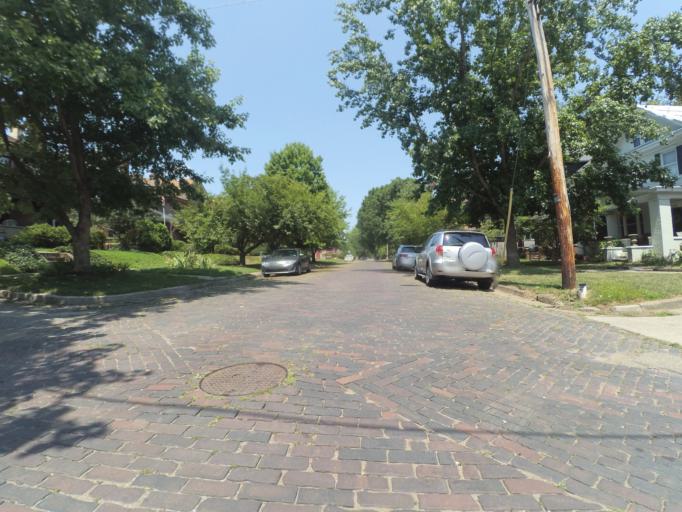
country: US
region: West Virginia
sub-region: Cabell County
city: Huntington
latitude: 38.4083
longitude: -82.4439
